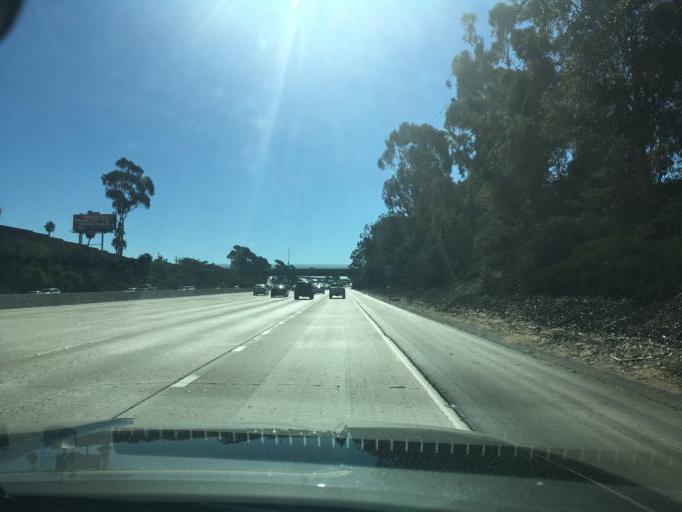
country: US
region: California
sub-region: San Diego County
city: National City
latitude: 32.6990
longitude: -117.0951
